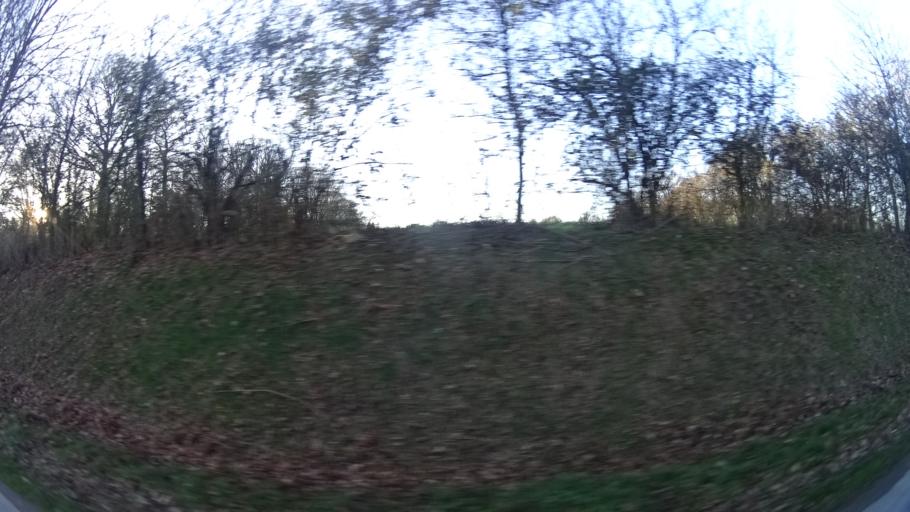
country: FR
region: Brittany
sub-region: Departement du Morbihan
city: Saint-Jean-la-Poterie
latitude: 47.6530
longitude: -2.1217
